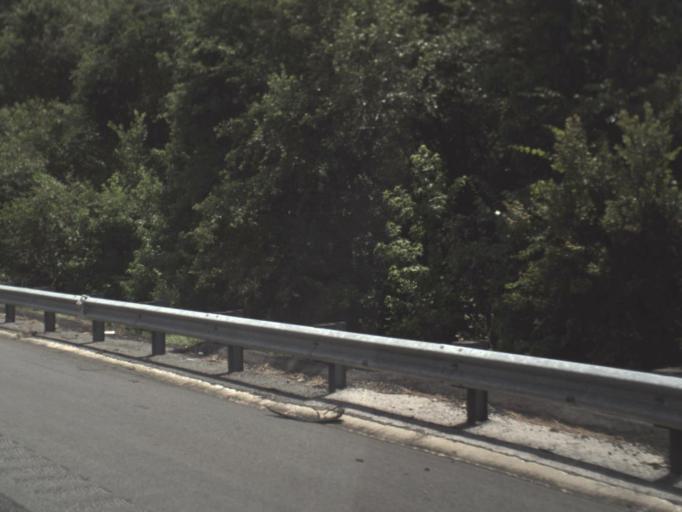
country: US
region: Florida
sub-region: Suwannee County
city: Live Oak
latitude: 30.3581
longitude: -83.1952
